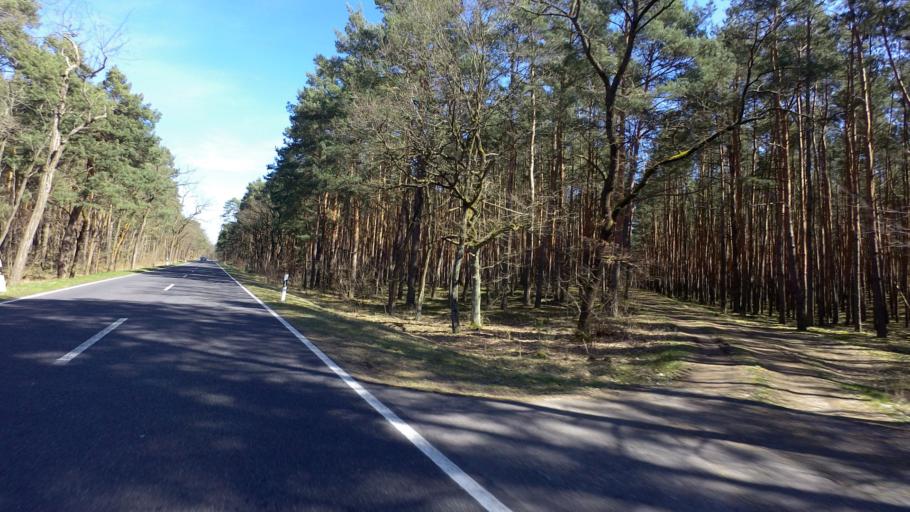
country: DE
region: Brandenburg
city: Munchehofe
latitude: 52.1315
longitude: 13.8211
